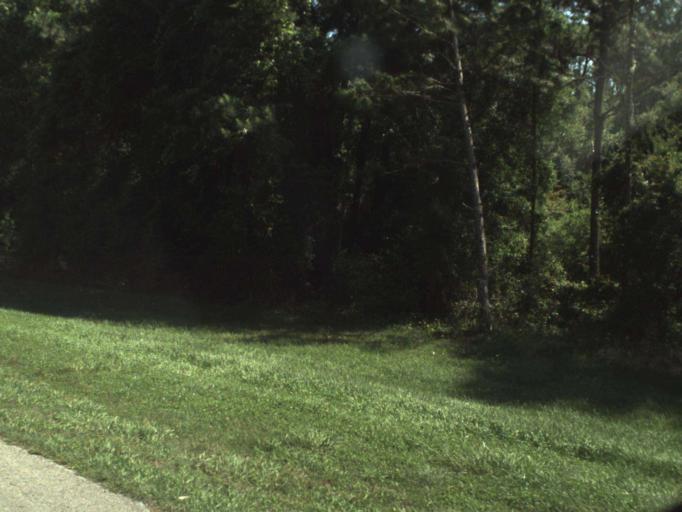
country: US
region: Florida
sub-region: Marion County
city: Belleview
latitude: 29.0961
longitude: -82.0857
